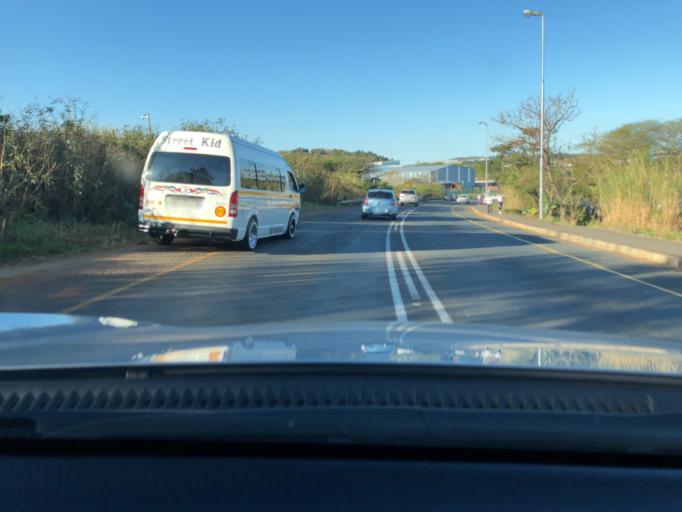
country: ZA
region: KwaZulu-Natal
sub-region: eThekwini Metropolitan Municipality
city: Umkomaas
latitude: -30.0291
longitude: 30.8811
